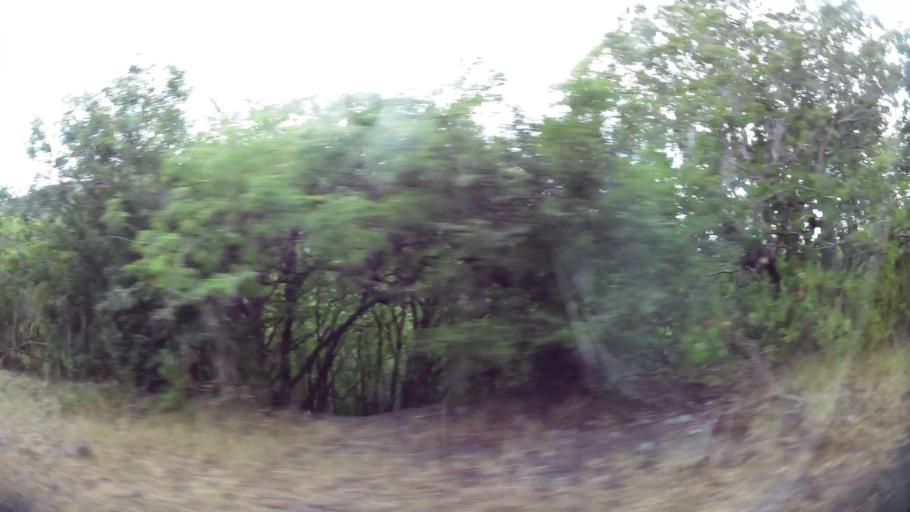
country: KN
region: Saint James Windwa
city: Newcastle
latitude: 17.2001
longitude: -62.5974
